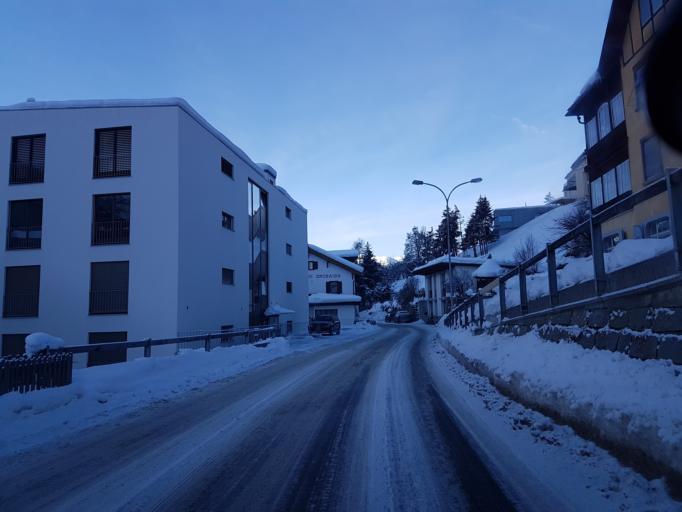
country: CH
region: Grisons
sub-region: Inn District
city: Scuol
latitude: 46.7999
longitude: 10.3064
